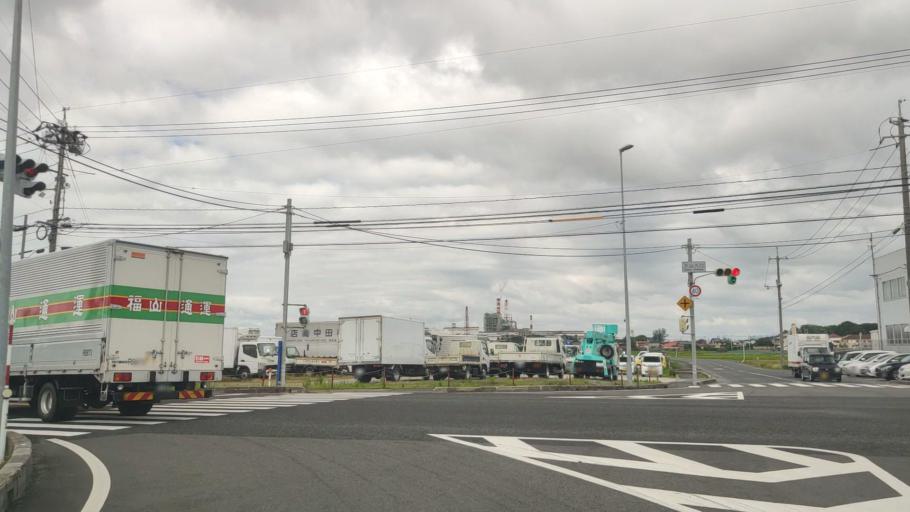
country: JP
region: Tottori
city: Yonago
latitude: 35.4358
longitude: 133.3879
